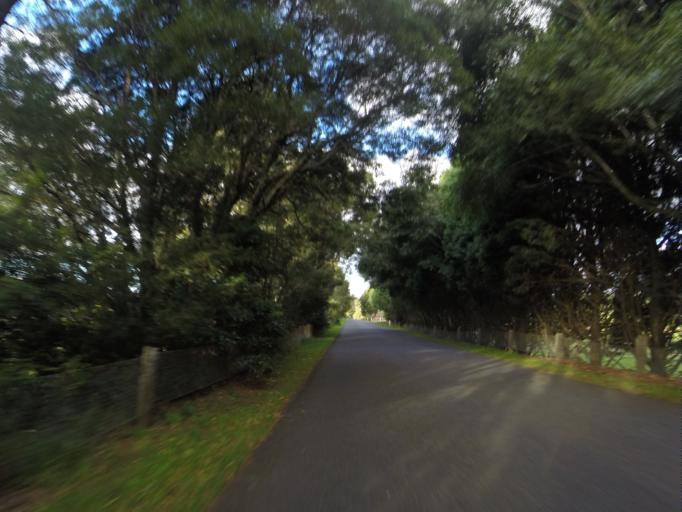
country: AU
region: New South Wales
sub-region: Shoalhaven Shire
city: Kangaroo Valley
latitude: -34.6026
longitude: 150.5487
